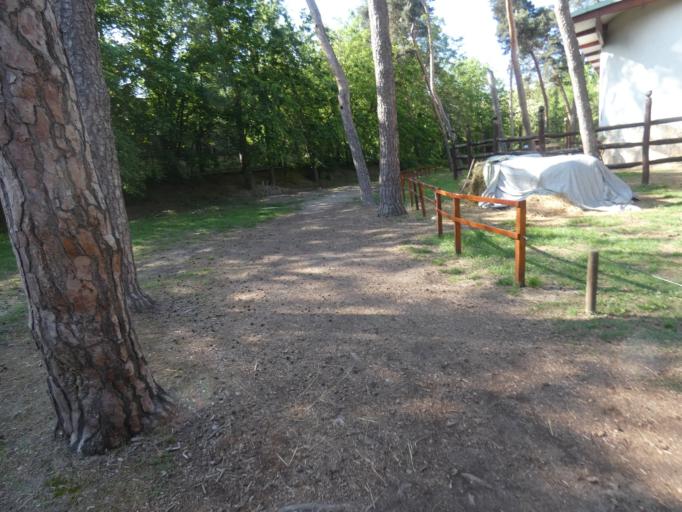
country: HU
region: Hajdu-Bihar
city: Debrecen
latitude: 47.5508
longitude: 21.6343
